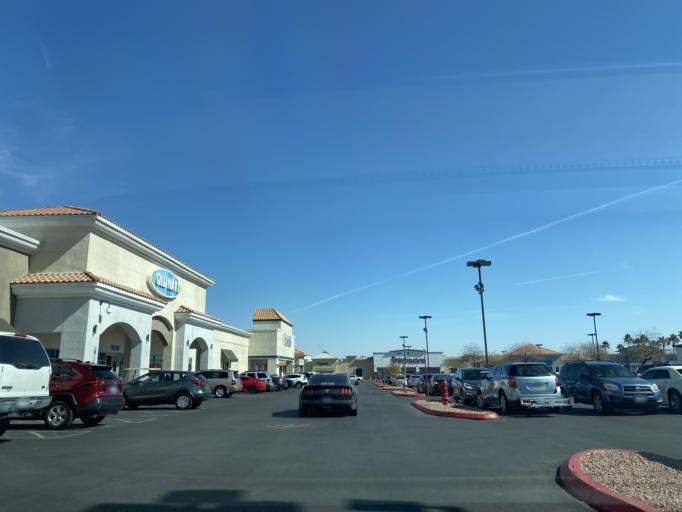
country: US
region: Nevada
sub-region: Clark County
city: Spring Valley
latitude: 36.1986
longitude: -115.2412
